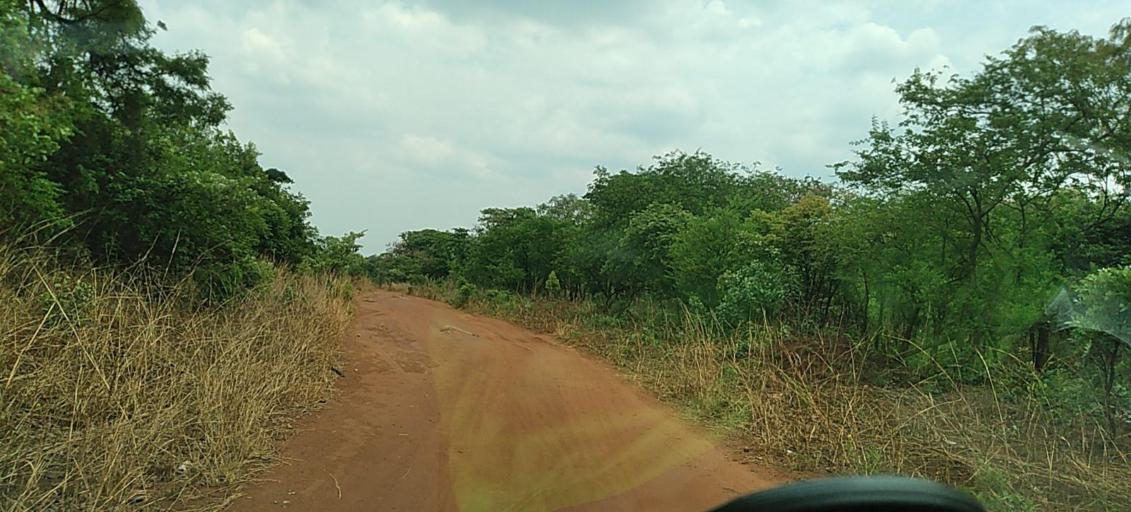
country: ZM
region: North-Western
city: Kansanshi
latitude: -12.0484
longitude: 26.3784
